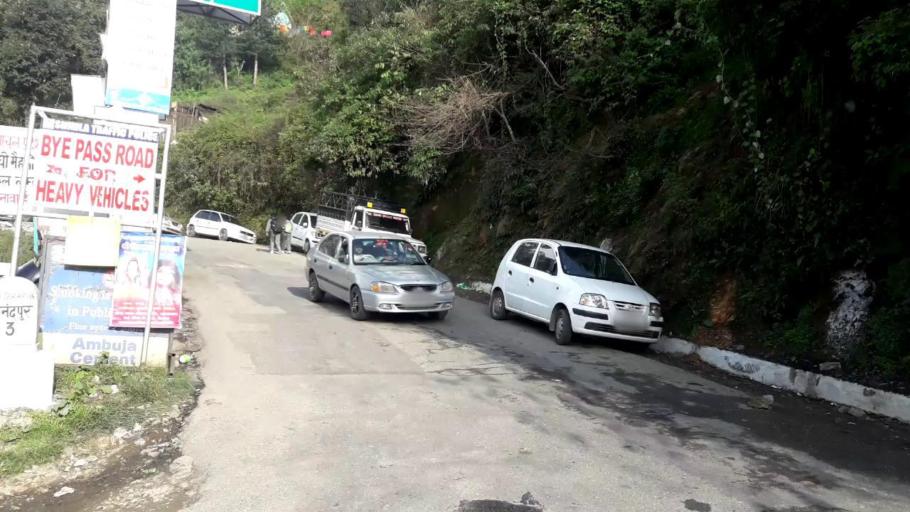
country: IN
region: Himachal Pradesh
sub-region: Shimla
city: Jutogh
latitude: 31.0419
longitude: 77.1271
